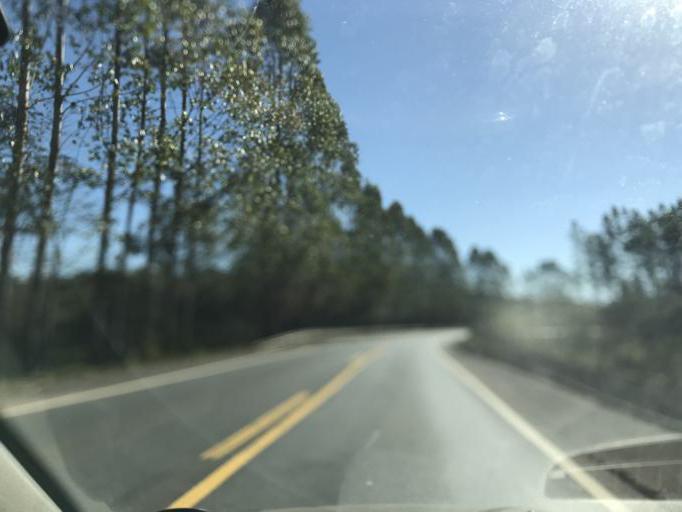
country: BR
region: Minas Gerais
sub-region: Bambui
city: Bambui
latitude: -19.8221
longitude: -46.0172
